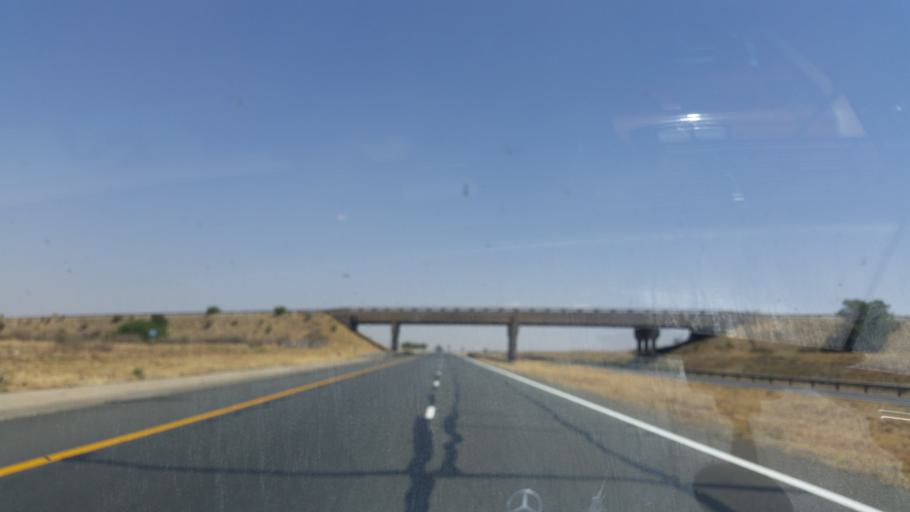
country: ZA
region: Orange Free State
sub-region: Lejweleputswa District Municipality
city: Brandfort
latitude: -28.8663
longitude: 26.5325
